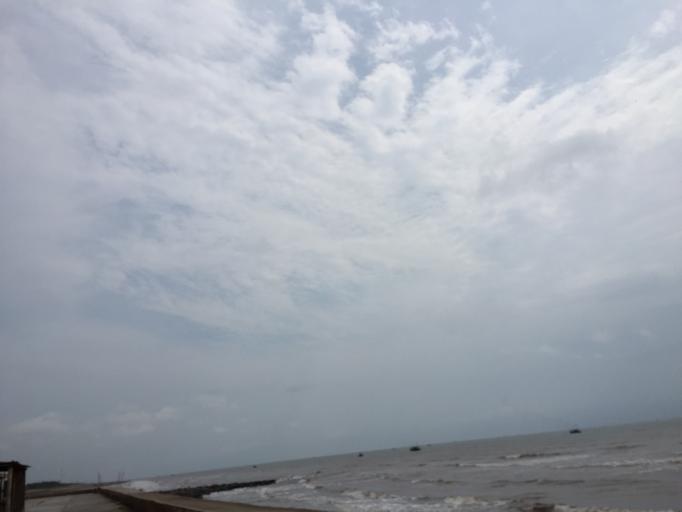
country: VN
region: Ninh Binh
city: Thi Tran Phat Diem
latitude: 20.0334
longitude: 106.2267
